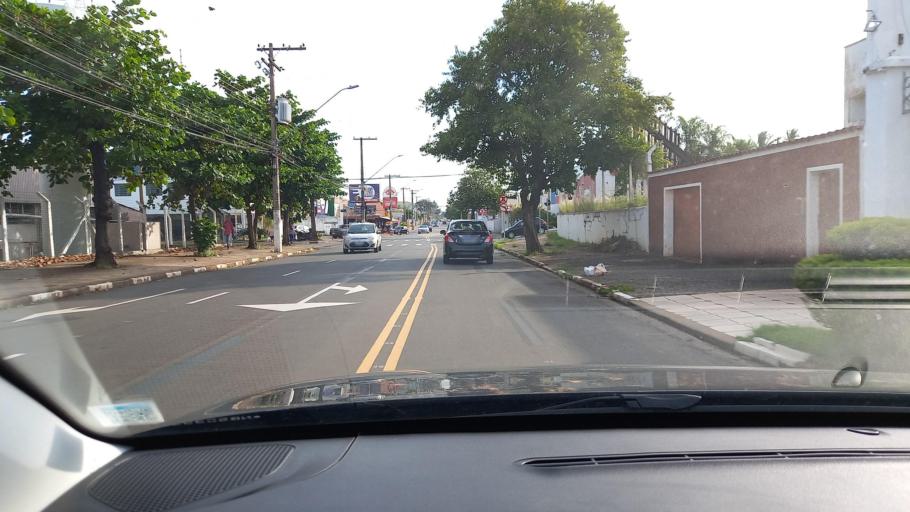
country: BR
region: Sao Paulo
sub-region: Mogi-Mirim
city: Mogi Mirim
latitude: -22.4413
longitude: -46.9677
